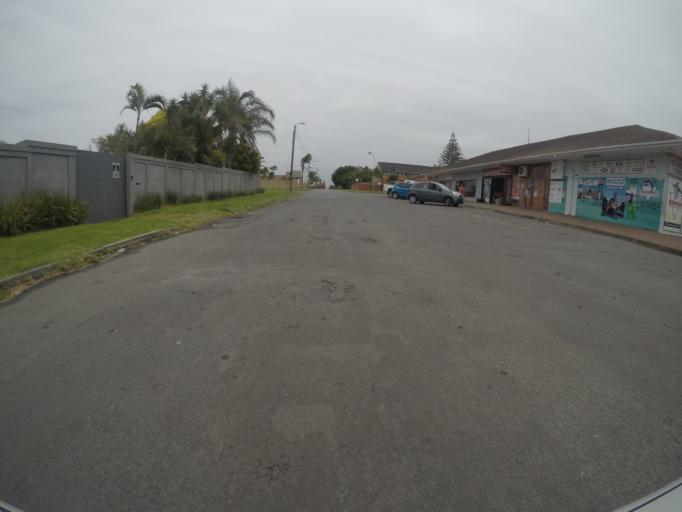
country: ZA
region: Eastern Cape
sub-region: Buffalo City Metropolitan Municipality
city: East London
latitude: -32.9642
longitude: 27.9325
